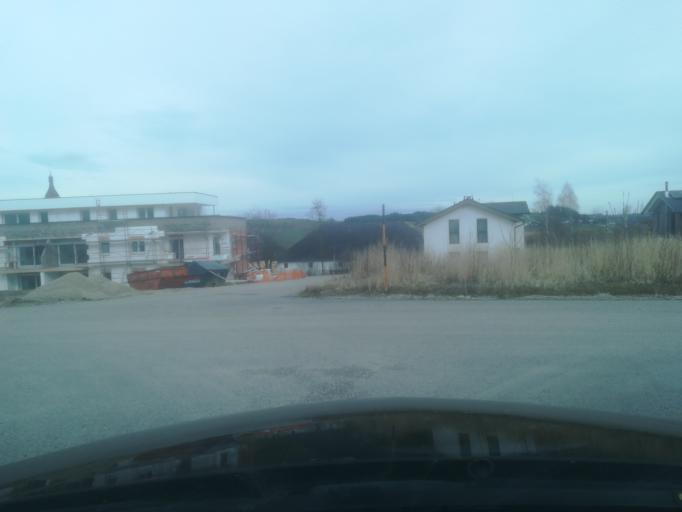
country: AT
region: Upper Austria
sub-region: Wels-Land
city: Neukirchen bei Lambach
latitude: 48.0986
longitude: 13.8137
